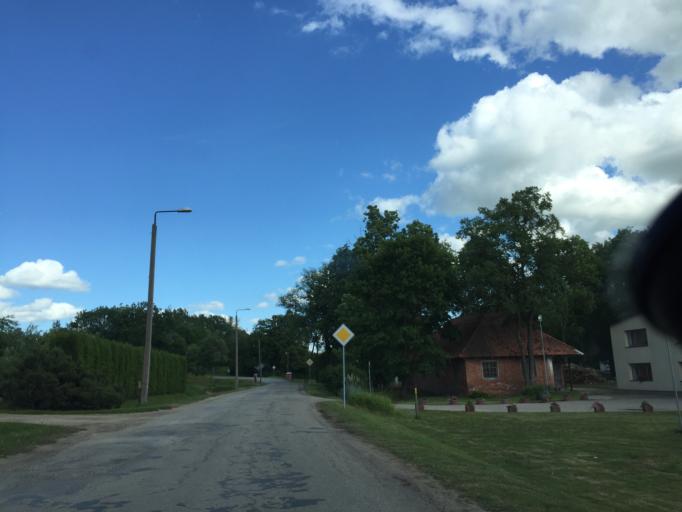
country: LT
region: Panevezys
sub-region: Birzai
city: Birzai
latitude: 56.3800
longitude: 24.6483
